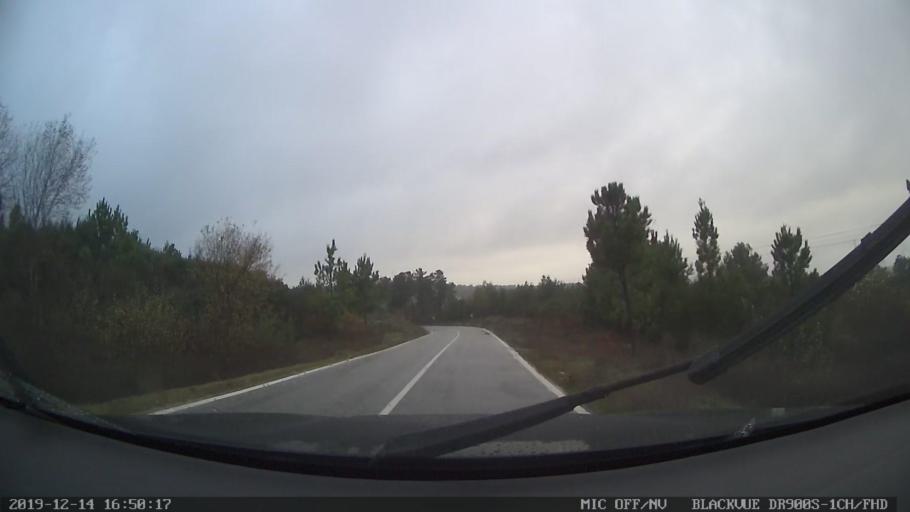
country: PT
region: Vila Real
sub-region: Murca
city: Murca
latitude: 41.4153
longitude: -7.5036
